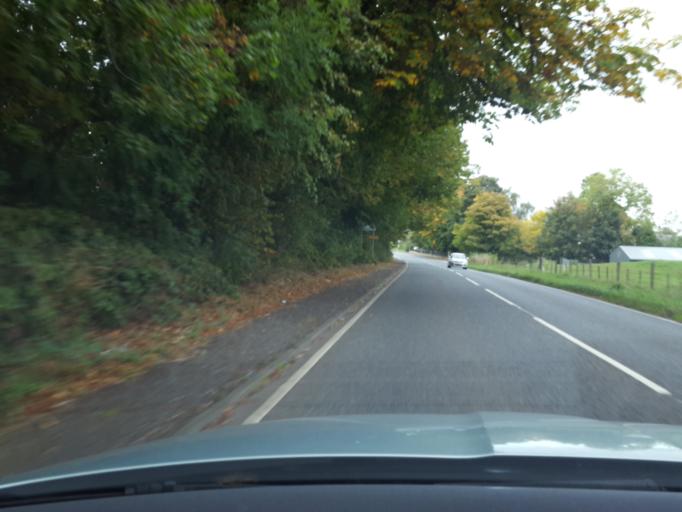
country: GB
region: Scotland
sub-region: Fife
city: Pathhead
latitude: 55.8698
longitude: -2.9909
